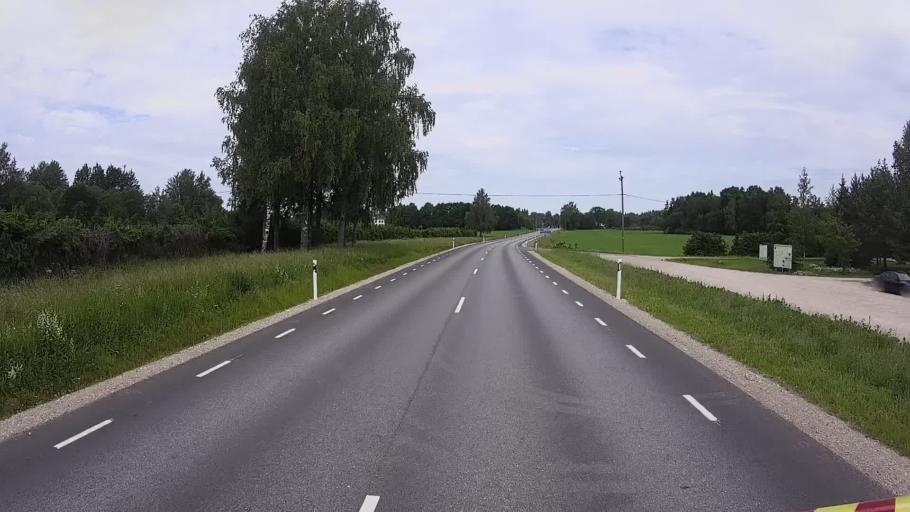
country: EE
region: Viljandimaa
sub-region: Viljandi linn
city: Viljandi
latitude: 58.2363
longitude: 25.5978
